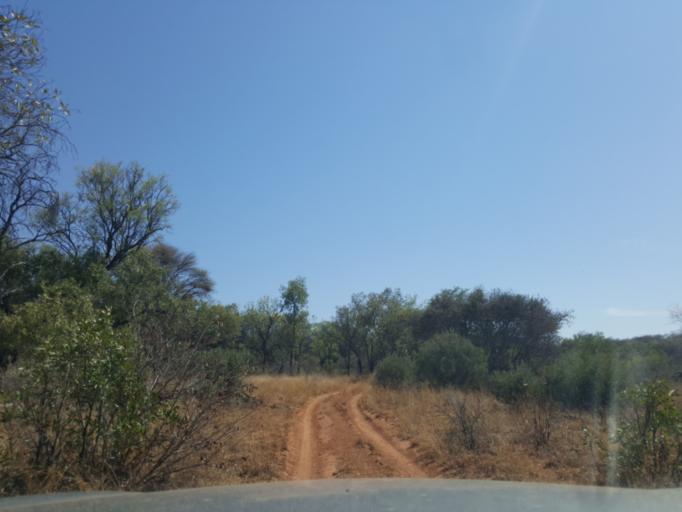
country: BW
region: South East
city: Lobatse
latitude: -25.1460
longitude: 25.6699
